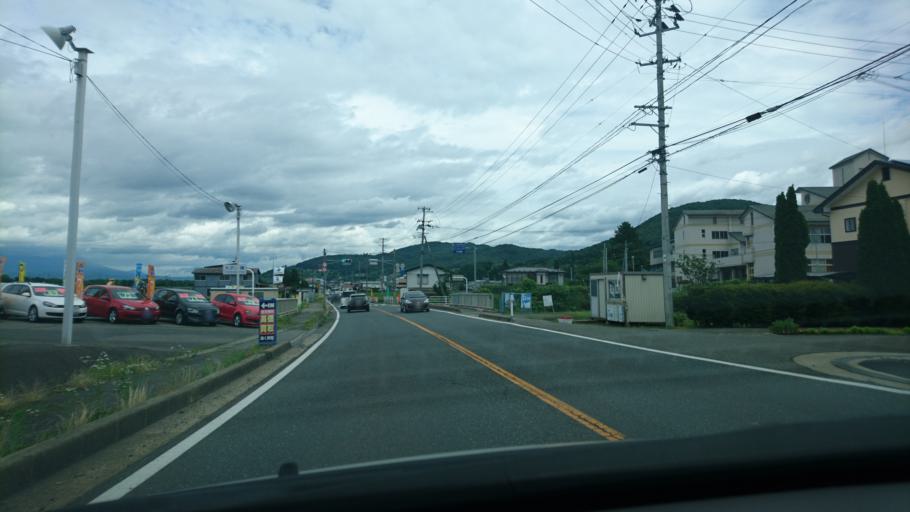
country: JP
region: Iwate
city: Morioka-shi
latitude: 39.6389
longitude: 141.1863
